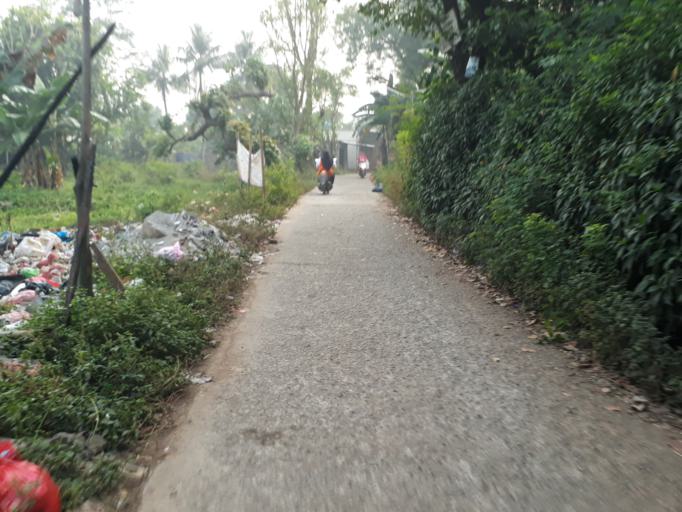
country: ID
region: West Java
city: Bekasi
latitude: -6.2487
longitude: 107.0675
